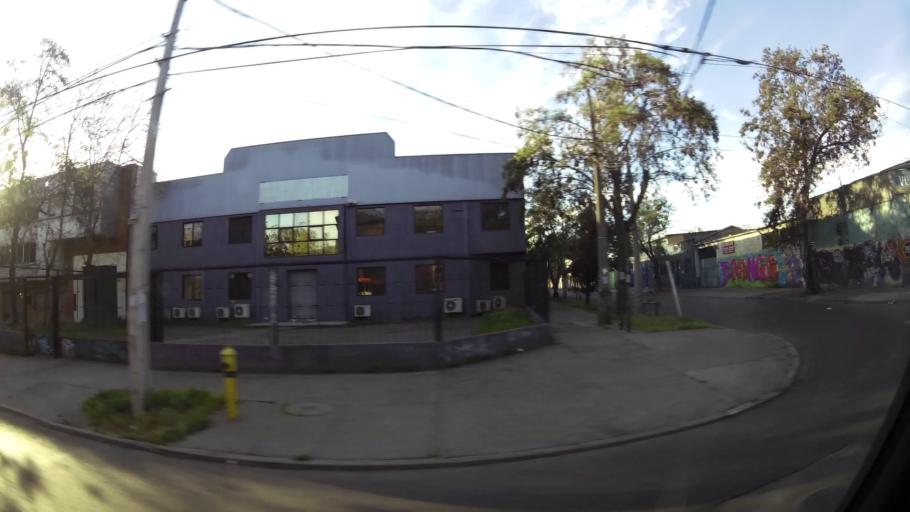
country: CL
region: Santiago Metropolitan
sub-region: Provincia de Santiago
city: Santiago
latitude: -33.4361
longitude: -70.6825
